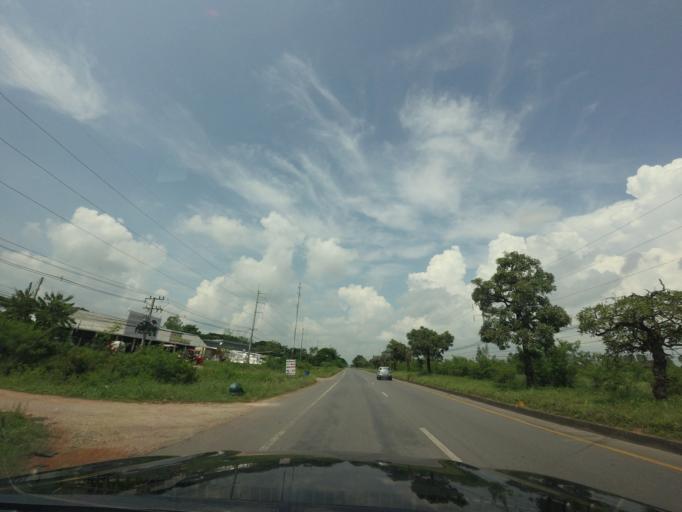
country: TH
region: Khon Kaen
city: Ban Fang
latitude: 16.4497
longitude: 102.7066
